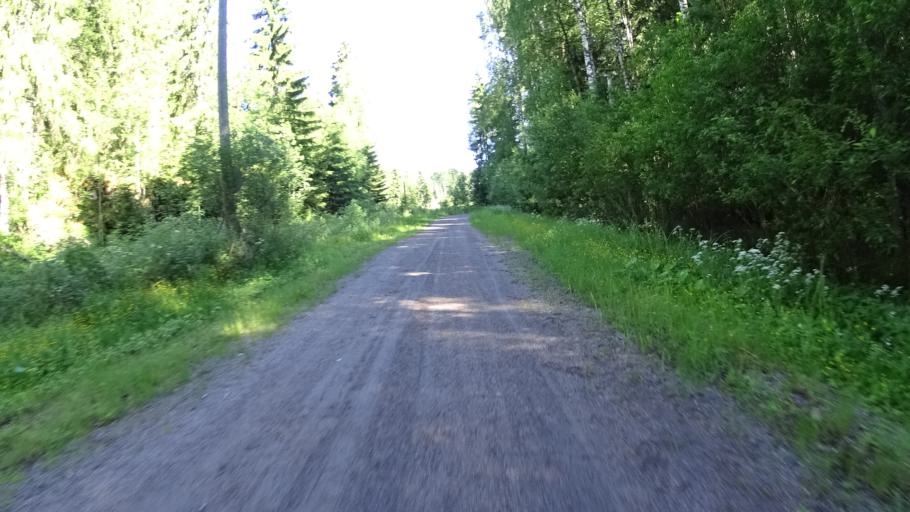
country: FI
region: Uusimaa
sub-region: Helsinki
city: Kilo
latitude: 60.3154
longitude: 24.8122
